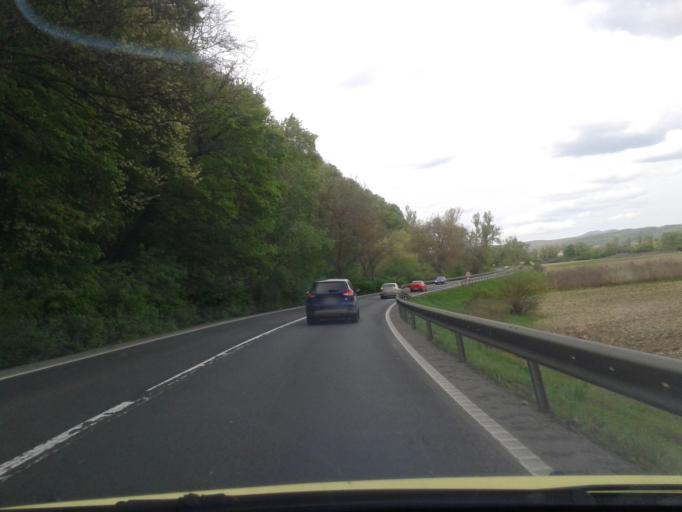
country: RO
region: Hunedoara
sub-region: Comuna Ilia
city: Ilia
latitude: 45.9206
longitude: 22.7026
